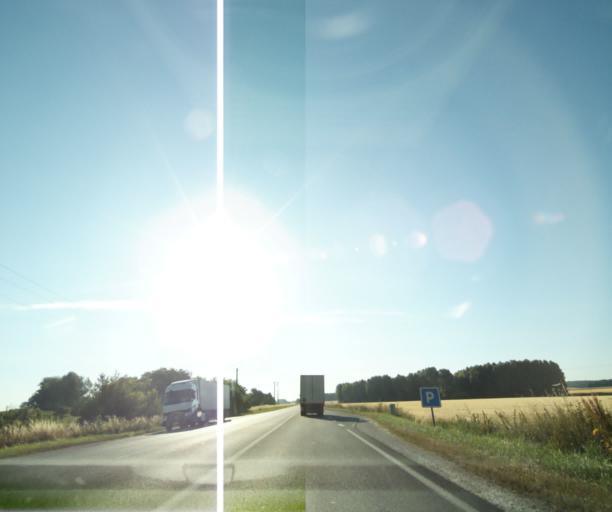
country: FR
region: Ile-de-France
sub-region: Departement de Seine-et-Marne
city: Varennes-sur-Seine
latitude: 48.3610
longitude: 2.9219
